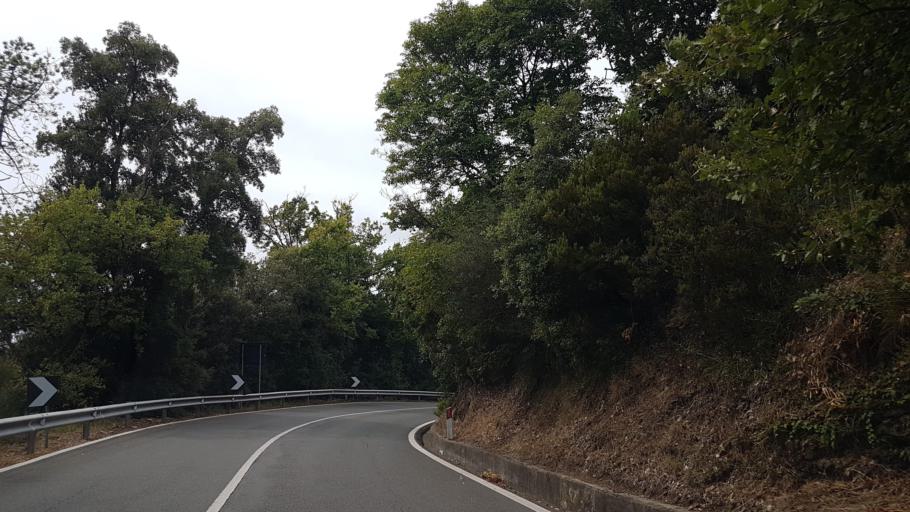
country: IT
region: Liguria
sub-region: Provincia di Genova
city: Moneglia
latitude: 44.2576
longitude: 9.4922
